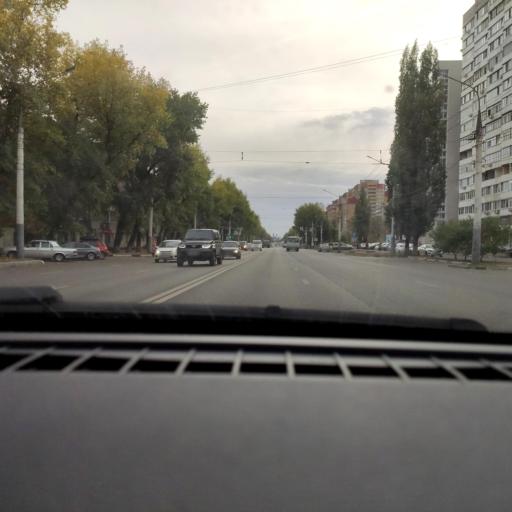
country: RU
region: Voronezj
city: Voronezh
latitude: 51.6479
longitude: 39.2400
